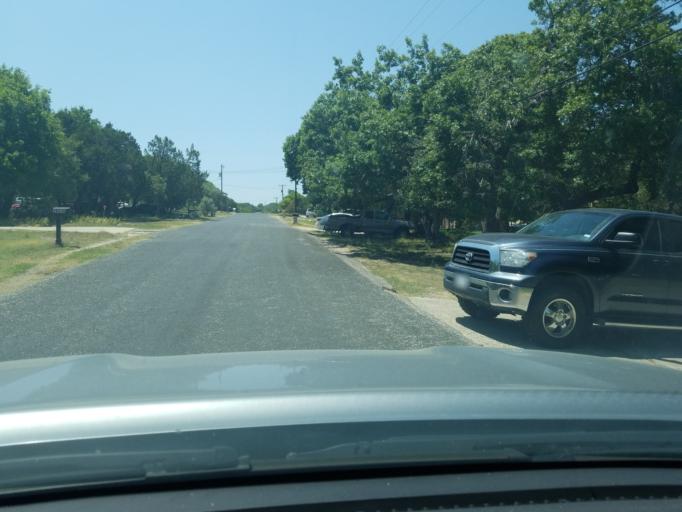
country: US
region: Texas
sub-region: Bexar County
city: Timberwood Park
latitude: 29.7152
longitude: -98.4924
